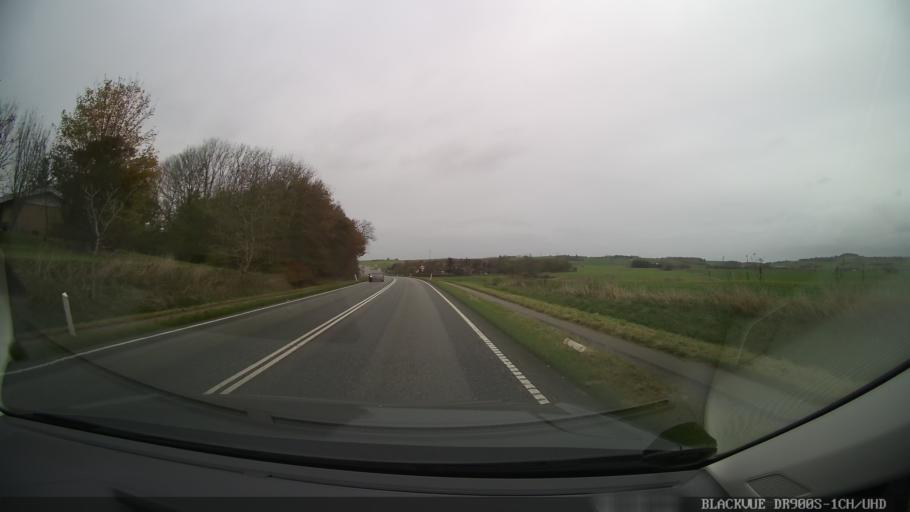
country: DK
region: North Denmark
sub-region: Thisted Kommune
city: Thisted
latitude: 56.8509
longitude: 8.7008
